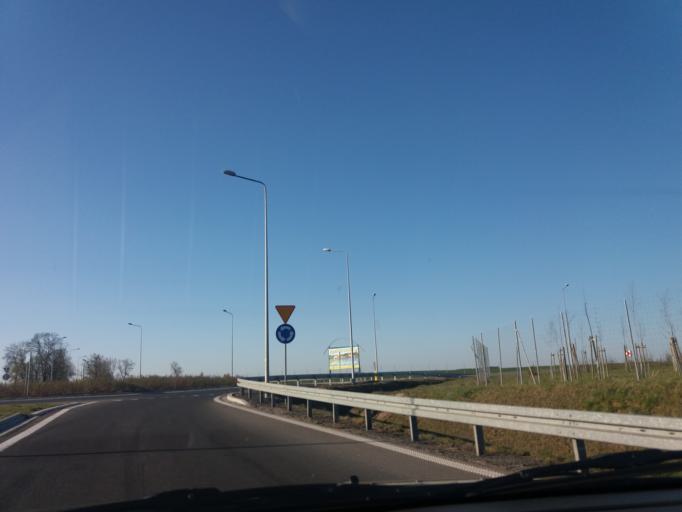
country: PL
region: Warmian-Masurian Voivodeship
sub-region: Powiat nidzicki
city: Nidzica
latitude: 53.3336
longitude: 20.4392
